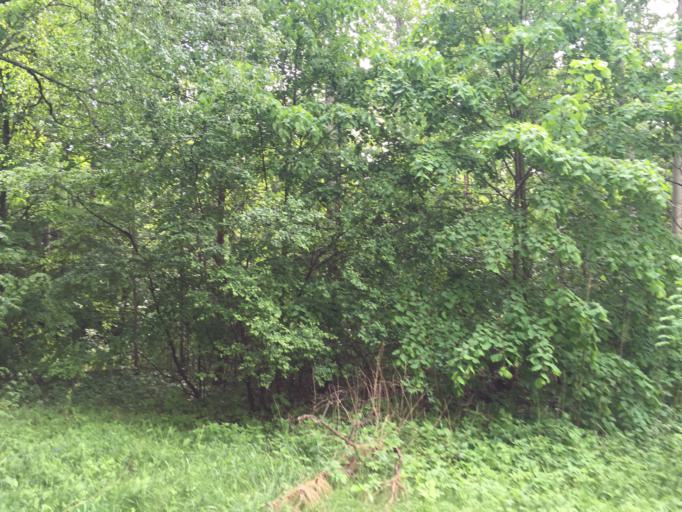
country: LT
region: Klaipedos apskritis
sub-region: Klaipeda
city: Klaipeda
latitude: 55.7712
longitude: 21.0853
